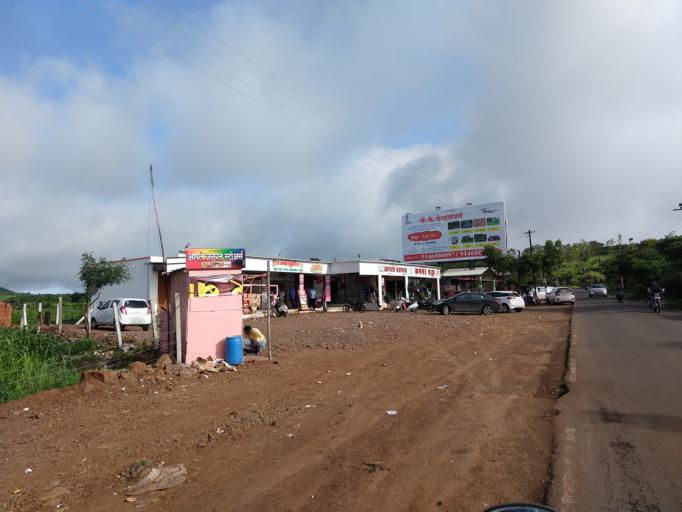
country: IN
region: Maharashtra
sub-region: Pune Division
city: Khed
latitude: 18.4020
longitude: 73.9119
